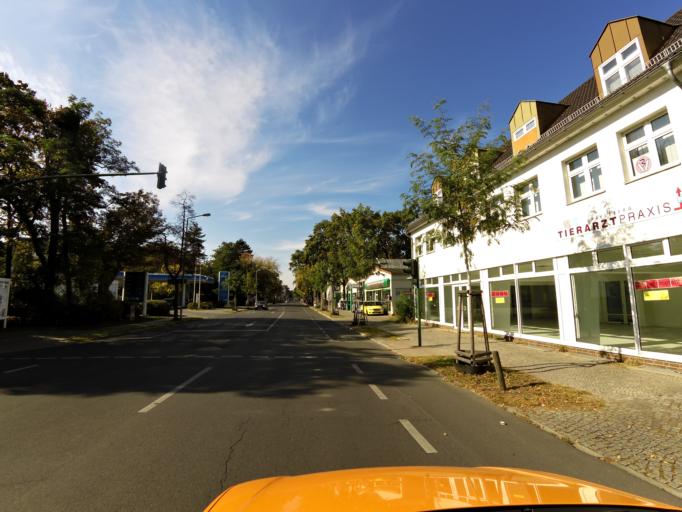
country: DE
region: Brandenburg
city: Potsdam
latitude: 52.3862
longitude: 13.1077
